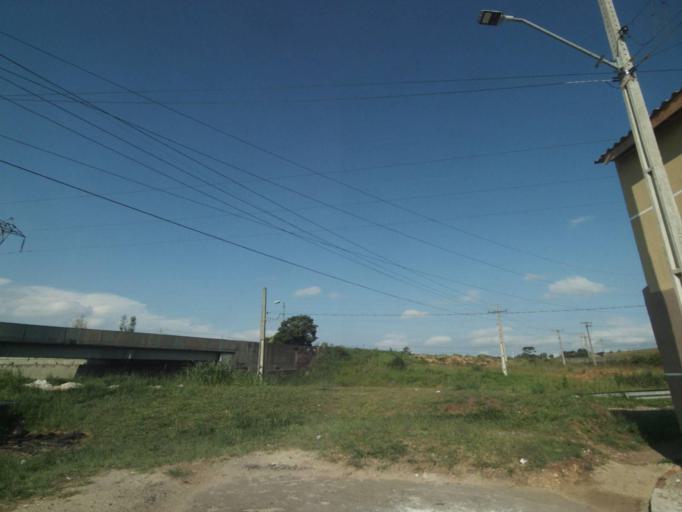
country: BR
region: Parana
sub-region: Araucaria
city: Araucaria
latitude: -25.5249
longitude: -49.3345
